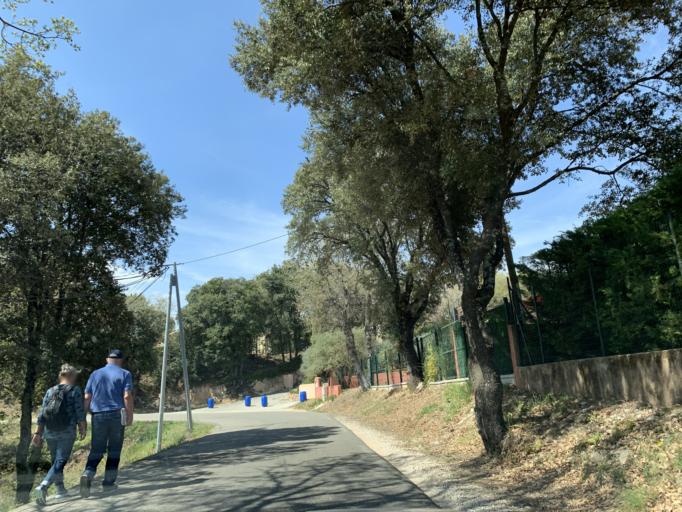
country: FR
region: Provence-Alpes-Cote d'Azur
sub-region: Departement du Vaucluse
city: Roussillon
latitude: 43.8950
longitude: 5.2928
